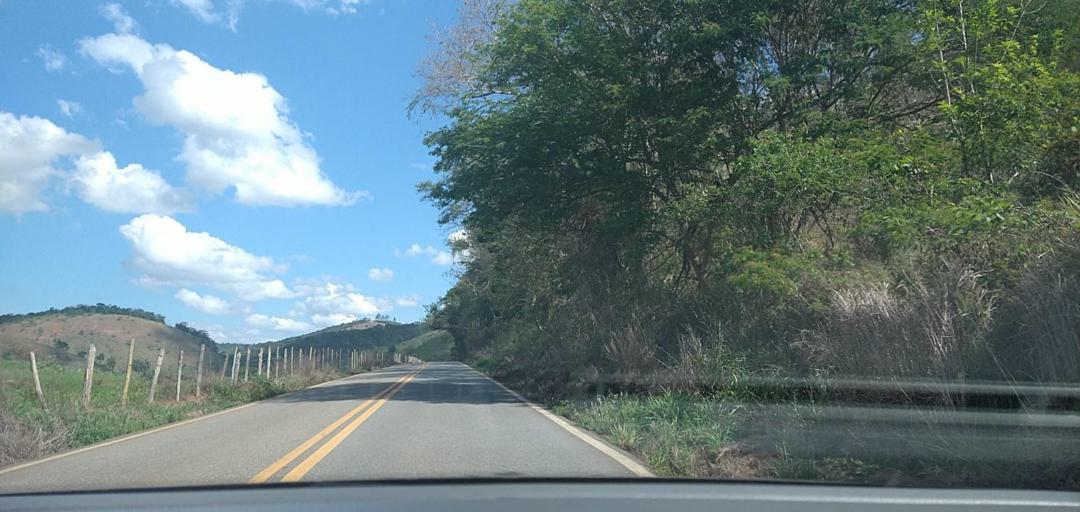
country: BR
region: Minas Gerais
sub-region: Rio Piracicaba
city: Rio Piracicaba
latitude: -19.9887
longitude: -43.1207
